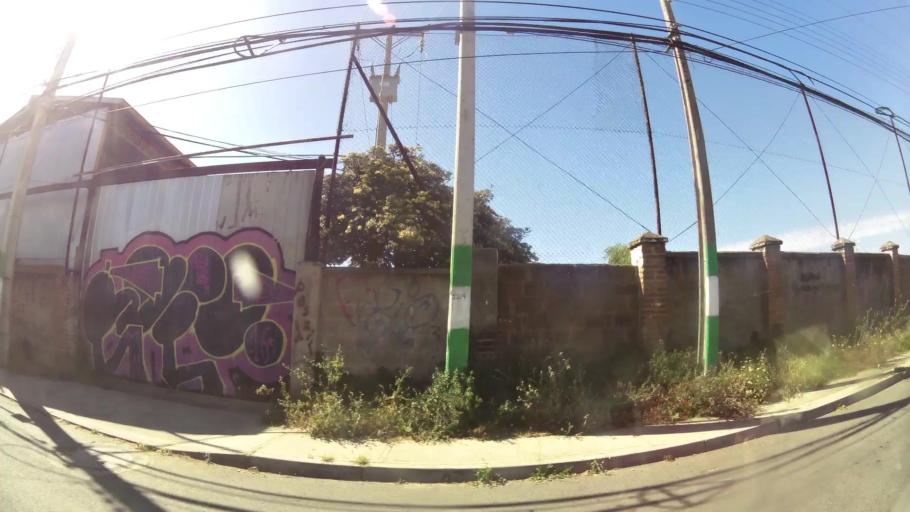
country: CL
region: Valparaiso
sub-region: Provincia de Valparaiso
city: Vina del Mar
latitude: -33.0334
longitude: -71.5712
